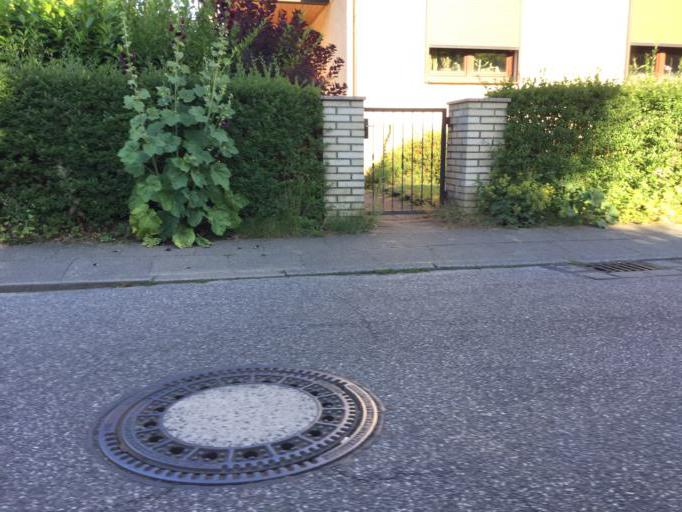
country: DE
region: Hamburg
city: Langenhorn
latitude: 53.6602
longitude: 10.0182
